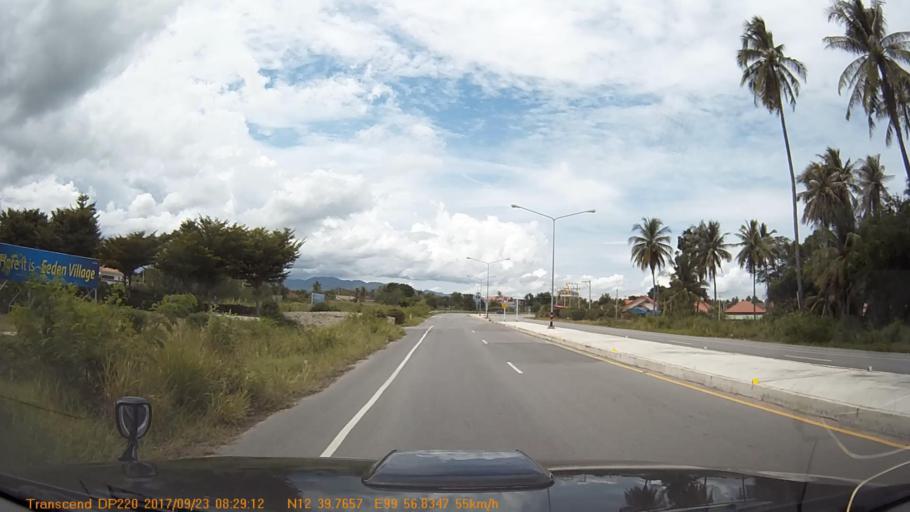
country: TH
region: Prachuap Khiri Khan
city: Hua Hin
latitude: 12.6627
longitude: 99.9473
